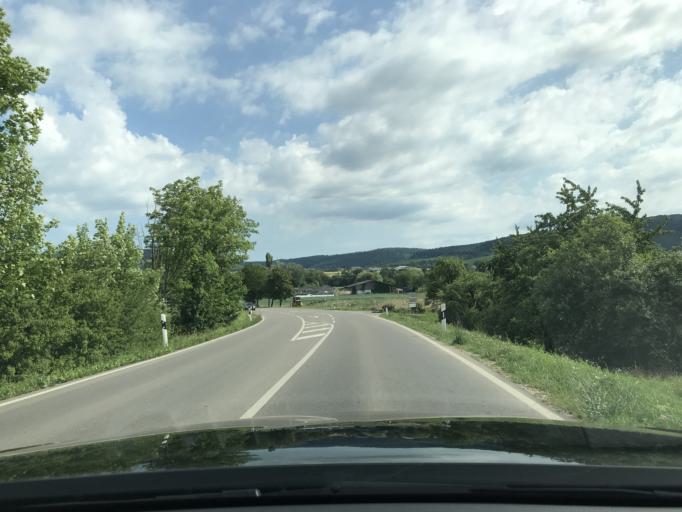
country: DE
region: Baden-Wuerttemberg
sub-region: Regierungsbezirk Stuttgart
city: Waiblingen
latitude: 48.8072
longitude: 9.3285
